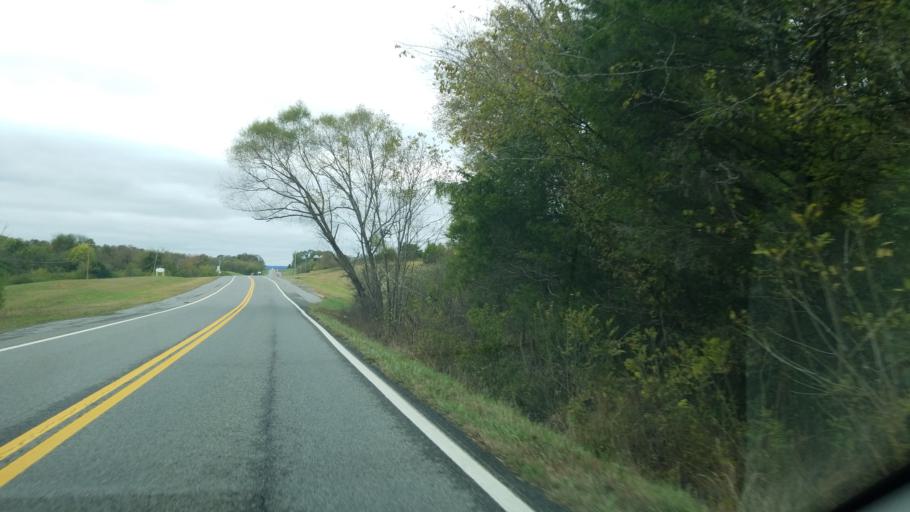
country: US
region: Tennessee
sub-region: Rhea County
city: Graysville
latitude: 35.3783
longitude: -84.9991
